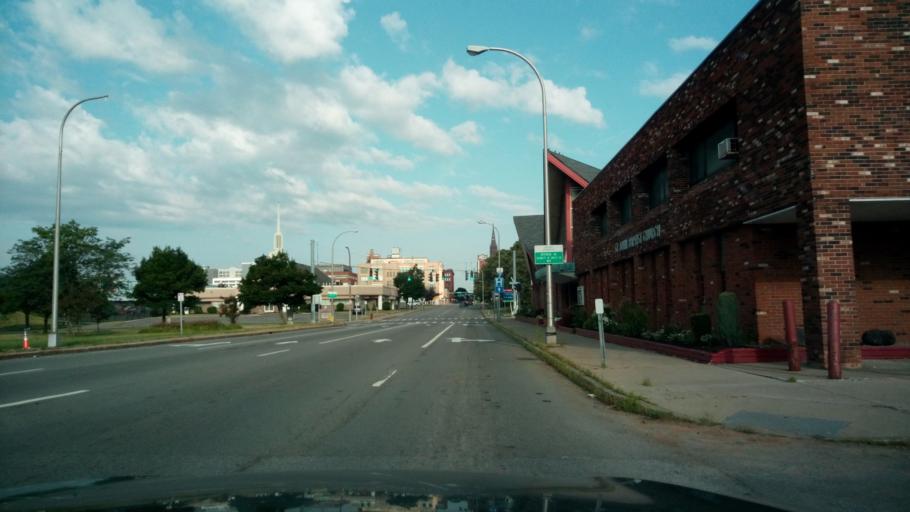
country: US
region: New York
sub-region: Erie County
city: Buffalo
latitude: 42.8941
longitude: -78.8638
